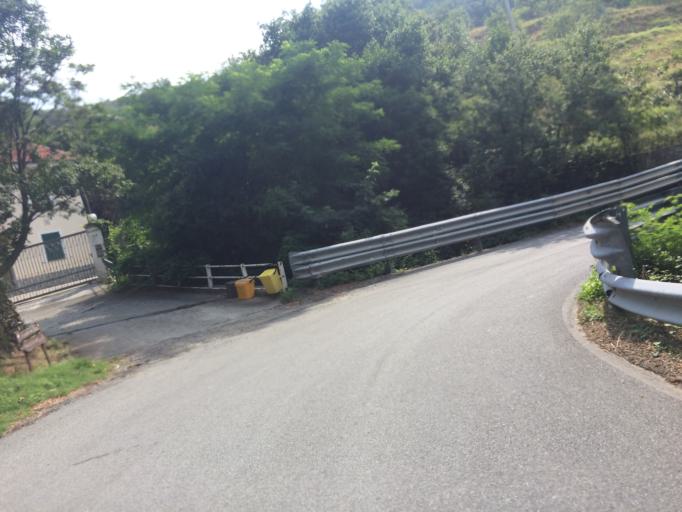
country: IT
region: Liguria
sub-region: Provincia di Savona
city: San Giovanni
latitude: 44.3942
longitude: 8.5104
